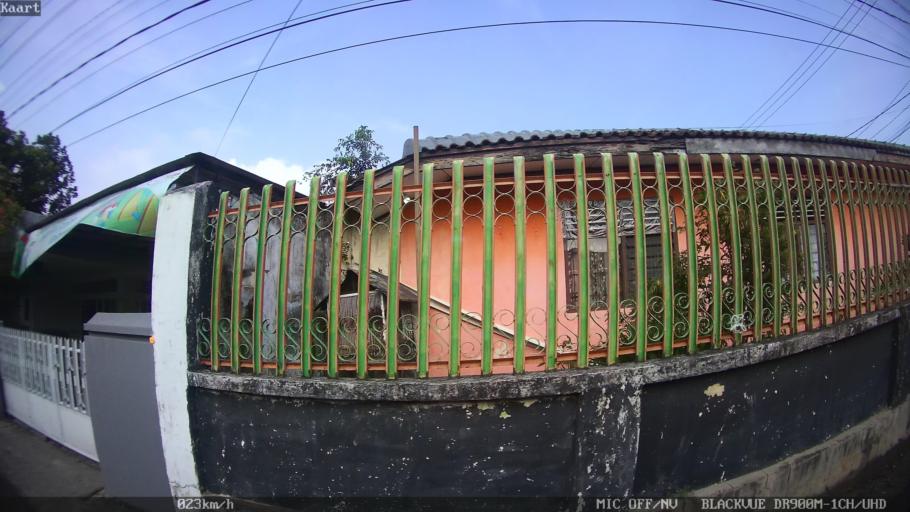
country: ID
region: Lampung
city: Kedaton
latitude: -5.3974
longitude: 105.2635
